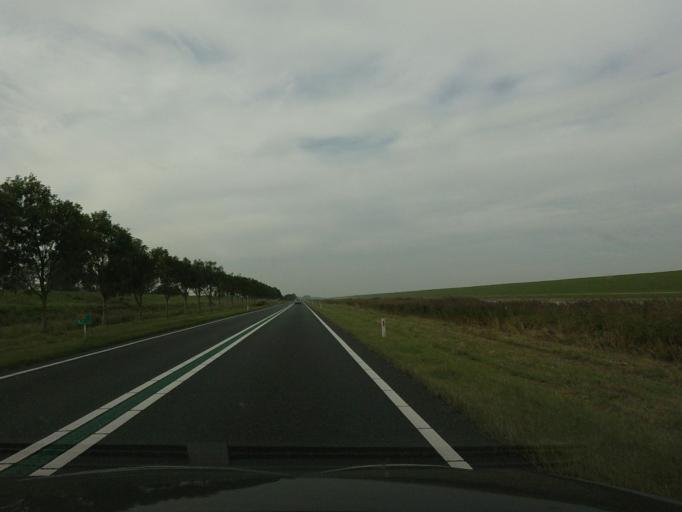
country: NL
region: North Holland
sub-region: Gemeente Den Helder
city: Den Helder
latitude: 52.8993
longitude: 4.8367
